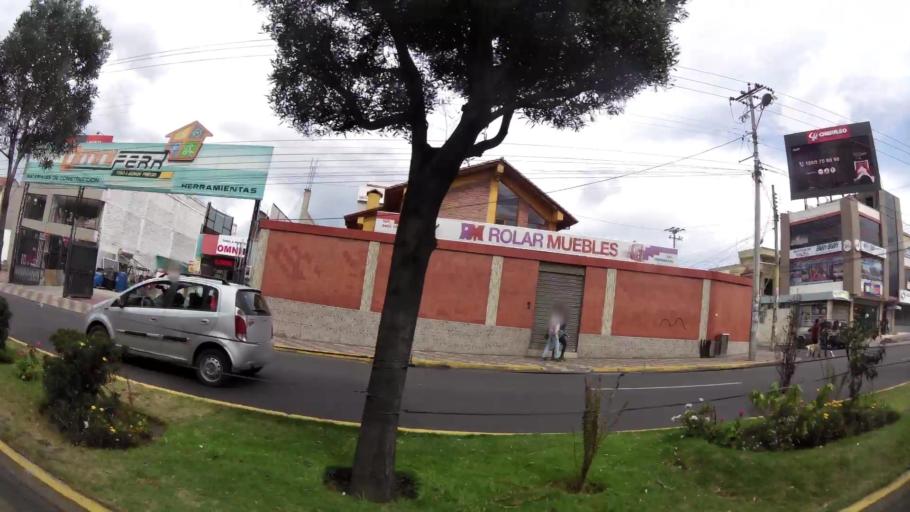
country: EC
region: Tungurahua
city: Ambato
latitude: -1.2661
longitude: -78.6274
